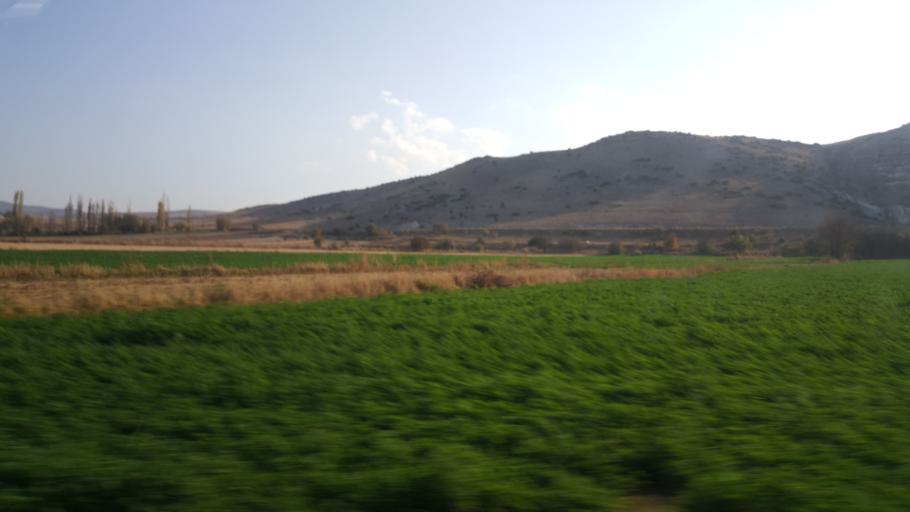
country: TR
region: Eskisehir
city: Seyitgazi
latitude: 39.4246
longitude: 30.6596
